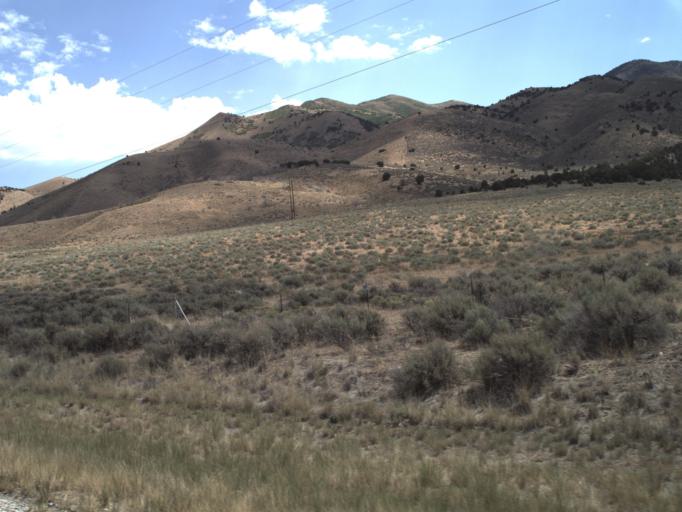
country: US
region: Utah
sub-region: Tooele County
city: Tooele
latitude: 40.4576
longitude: -112.3586
